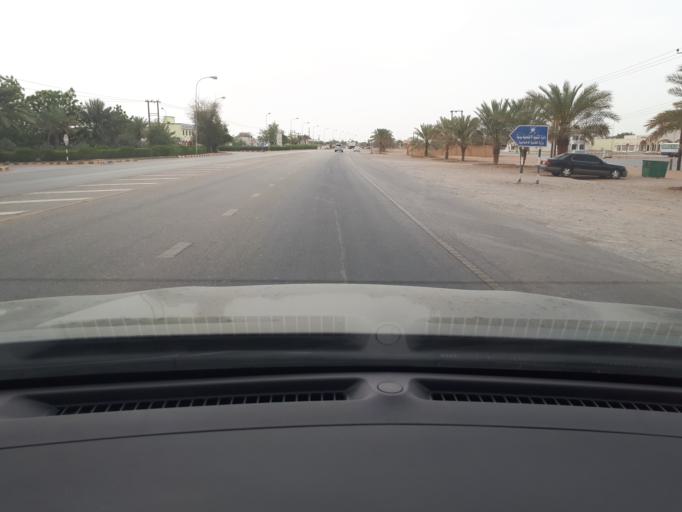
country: OM
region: Ash Sharqiyah
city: Badiyah
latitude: 22.4519
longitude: 58.8124
